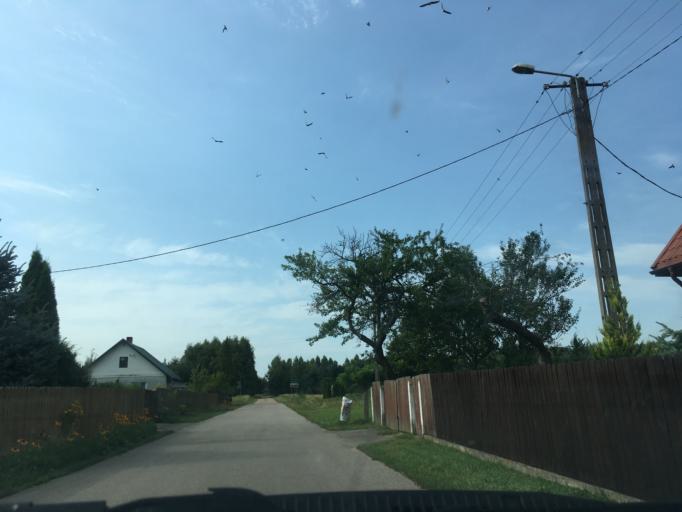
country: PL
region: Podlasie
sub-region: Powiat hajnowski
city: Bialowieza
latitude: 52.8884
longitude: 23.8517
